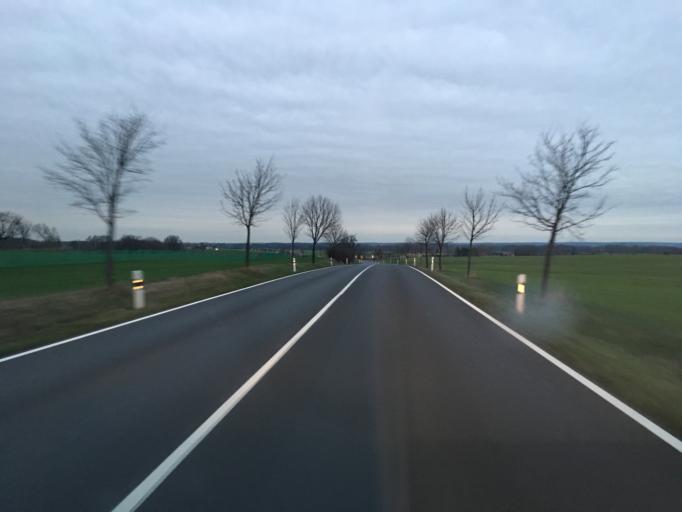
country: DE
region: Saxony
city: Oschatz
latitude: 51.3107
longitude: 13.0848
